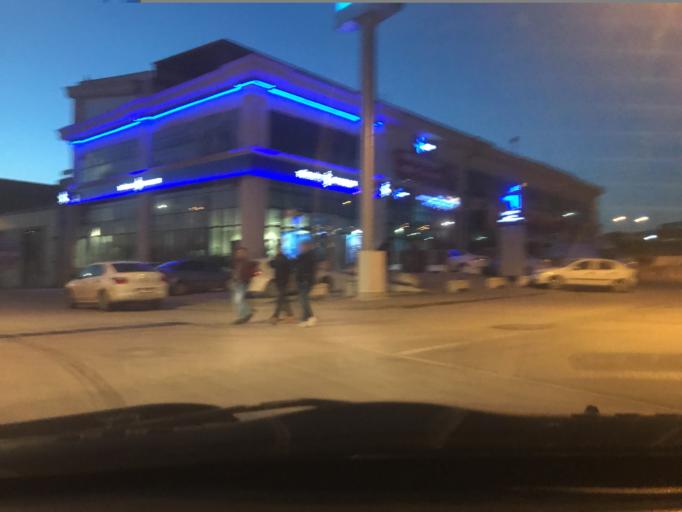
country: TR
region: Ankara
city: Batikent
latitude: 39.9728
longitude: 32.7398
